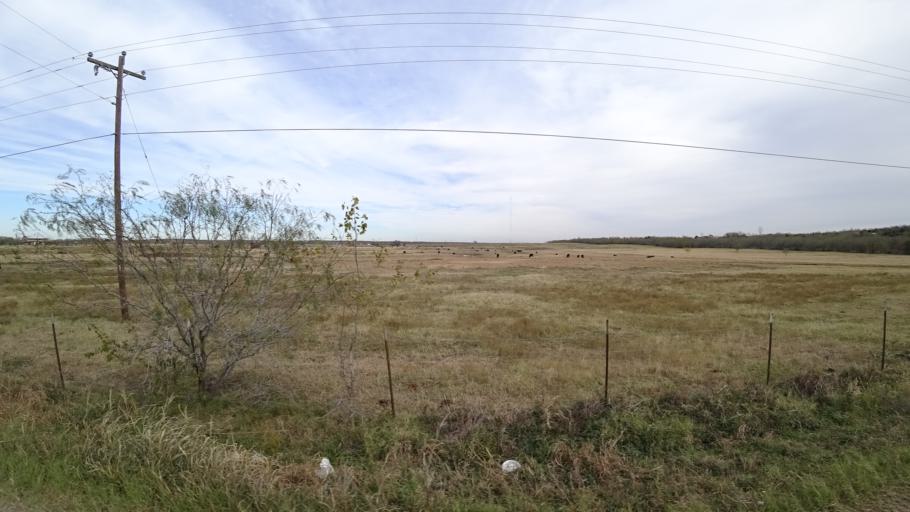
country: US
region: Texas
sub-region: Travis County
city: Garfield
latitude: 30.1156
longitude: -97.5891
